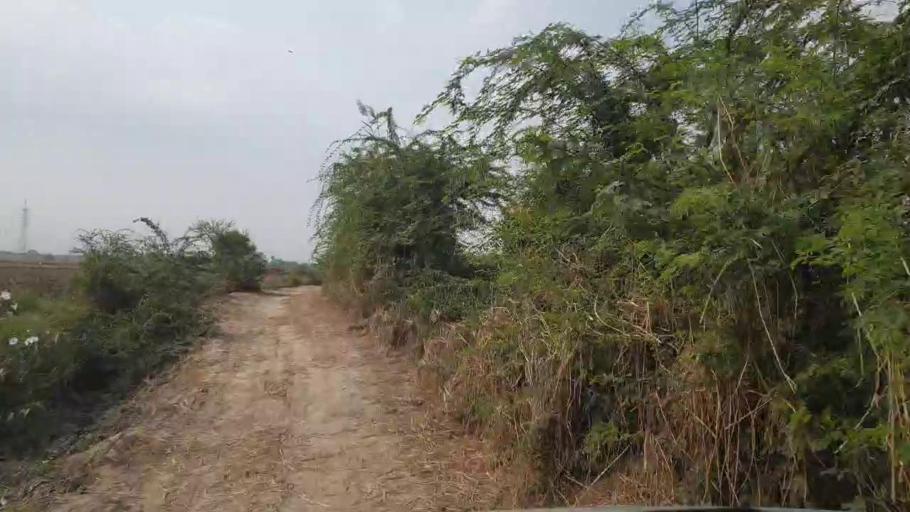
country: PK
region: Sindh
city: Talhar
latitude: 24.8833
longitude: 68.7941
